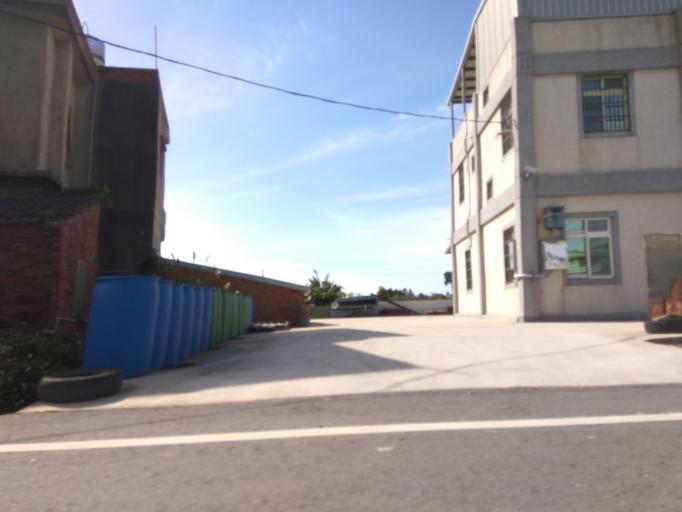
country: TW
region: Taiwan
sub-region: Hsinchu
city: Zhubei
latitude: 24.9952
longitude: 121.0441
